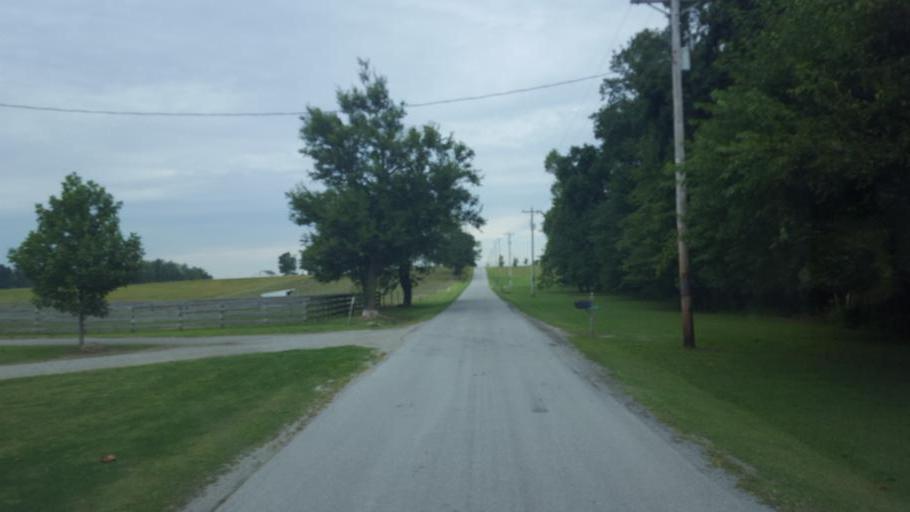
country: US
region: Ohio
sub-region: Wyandot County
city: Upper Sandusky
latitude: 40.7809
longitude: -83.1884
